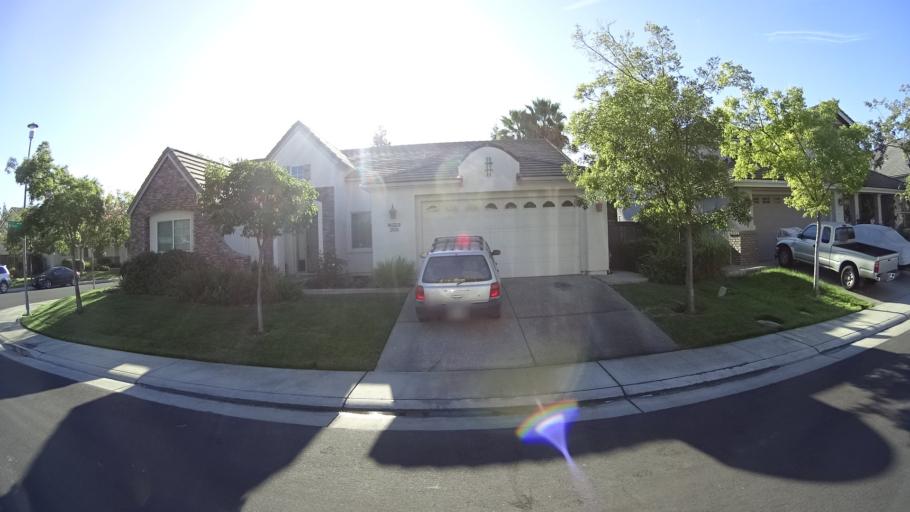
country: US
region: California
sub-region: Sacramento County
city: Laguna
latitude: 38.4000
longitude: -121.4695
